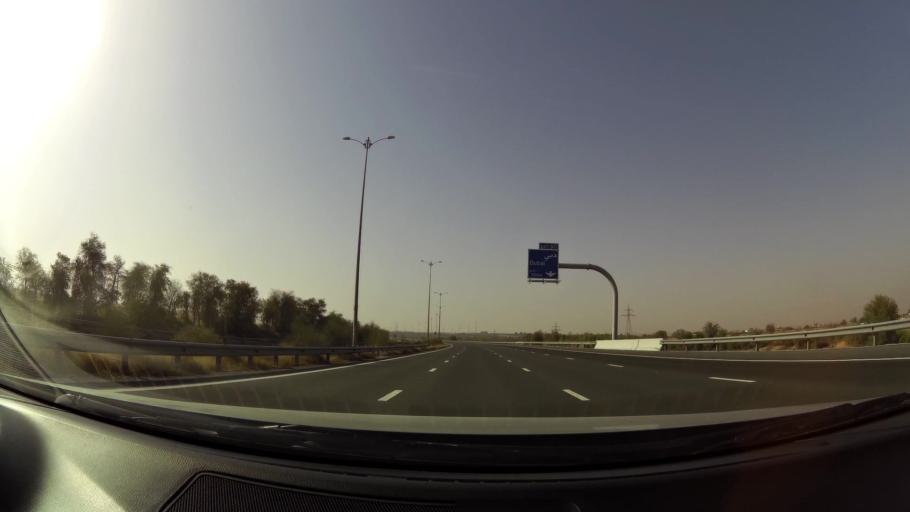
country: OM
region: Al Buraimi
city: Al Buraymi
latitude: 24.6476
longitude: 55.7045
